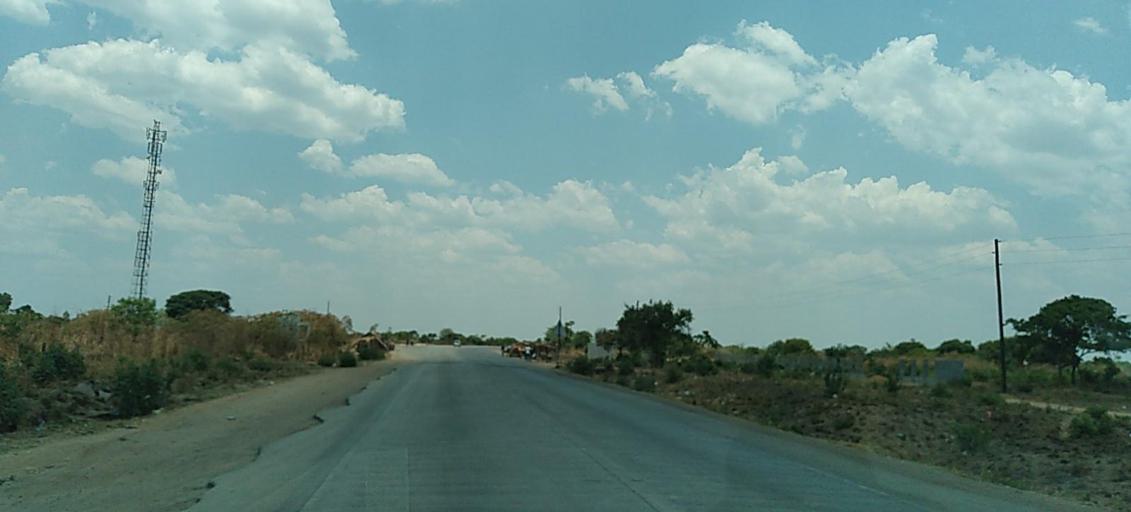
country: ZM
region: Central
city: Kapiri Mposhi
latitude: -13.8928
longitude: 28.6586
